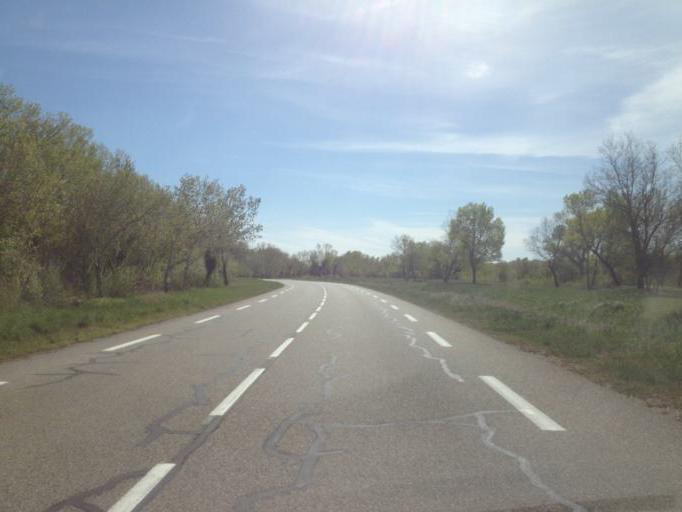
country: FR
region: Provence-Alpes-Cote d'Azur
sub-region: Departement du Vaucluse
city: Caderousse
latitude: 44.0929
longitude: 4.7317
